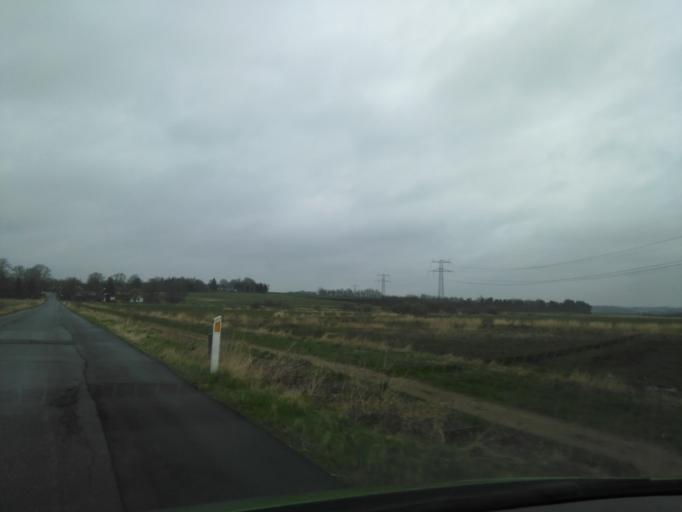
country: DK
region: Central Jutland
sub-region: Arhus Kommune
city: Framlev
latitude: 56.1321
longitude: 10.0404
